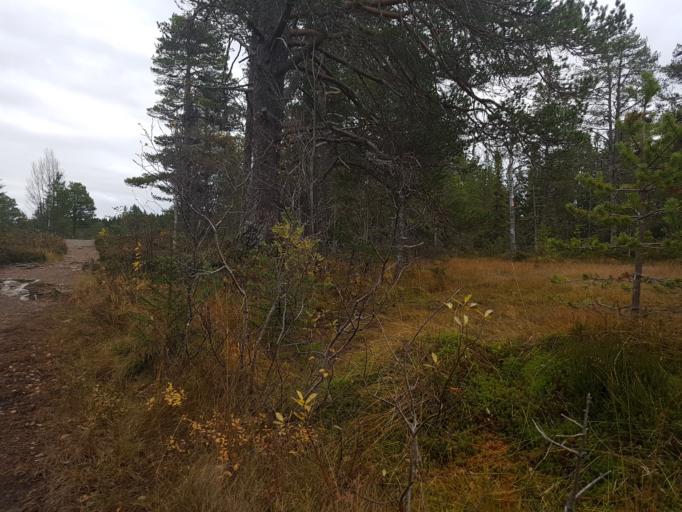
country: NO
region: Sor-Trondelag
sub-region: Melhus
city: Melhus
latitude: 63.3846
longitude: 10.2438
